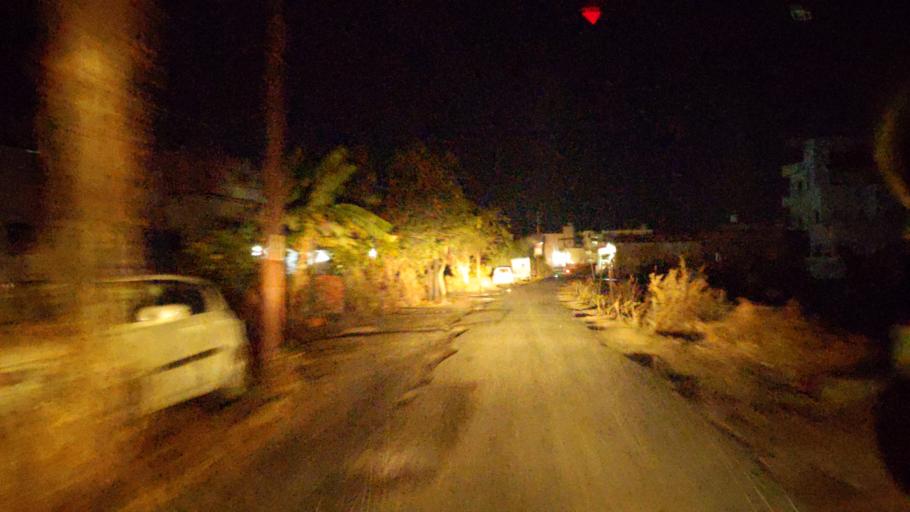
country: IN
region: Uttarakhand
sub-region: Naini Tal
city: Haldwani
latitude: 29.2073
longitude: 79.4995
